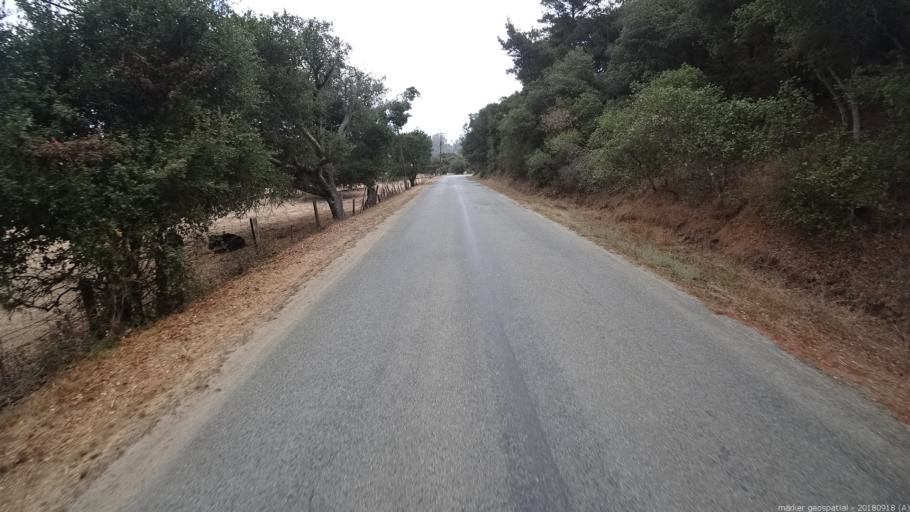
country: US
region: California
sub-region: Monterey County
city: Prunedale
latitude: 36.7830
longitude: -121.6335
